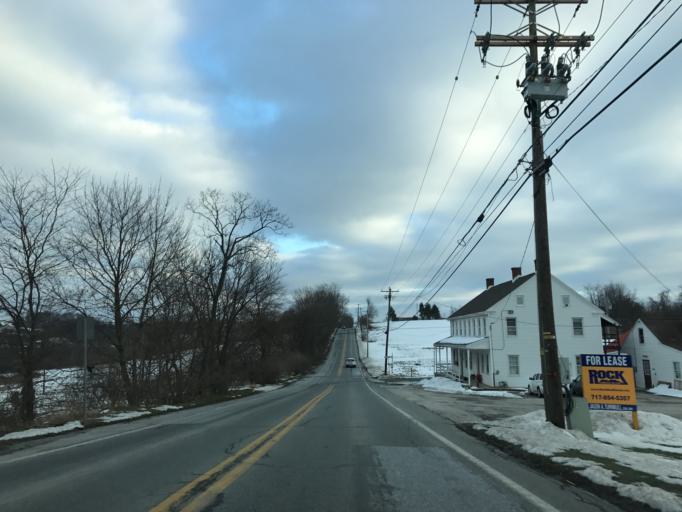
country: US
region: Pennsylvania
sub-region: York County
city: Loganville
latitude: 39.8198
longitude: -76.6931
